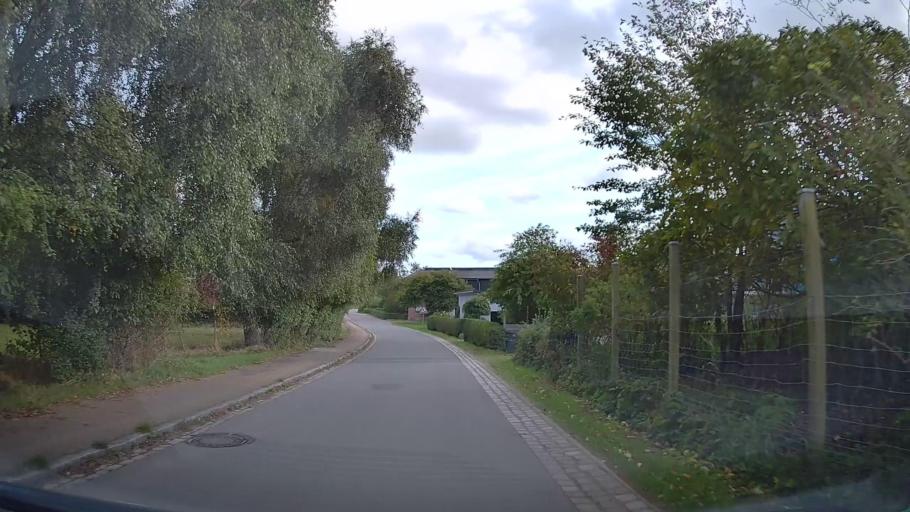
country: DE
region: Schleswig-Holstein
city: Steinberg
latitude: 54.7715
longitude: 9.8054
